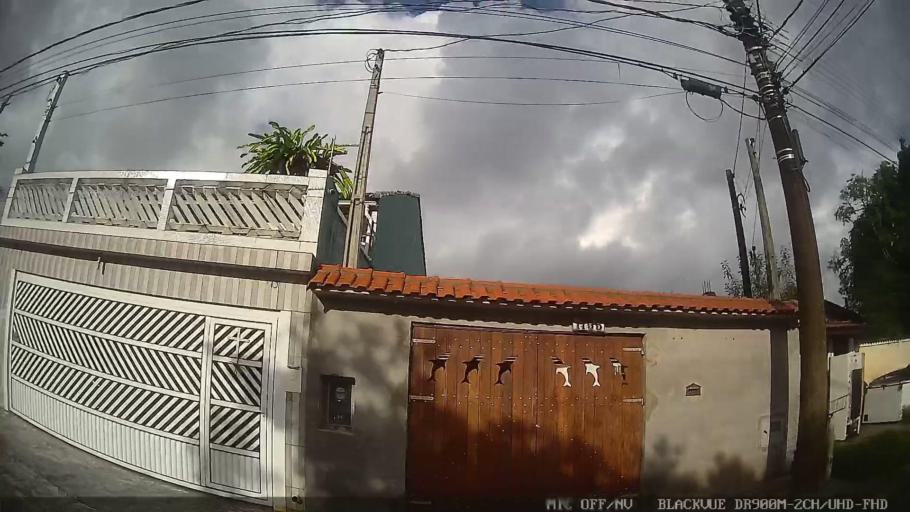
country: BR
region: Sao Paulo
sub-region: Itanhaem
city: Itanhaem
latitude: -24.2271
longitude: -46.8918
